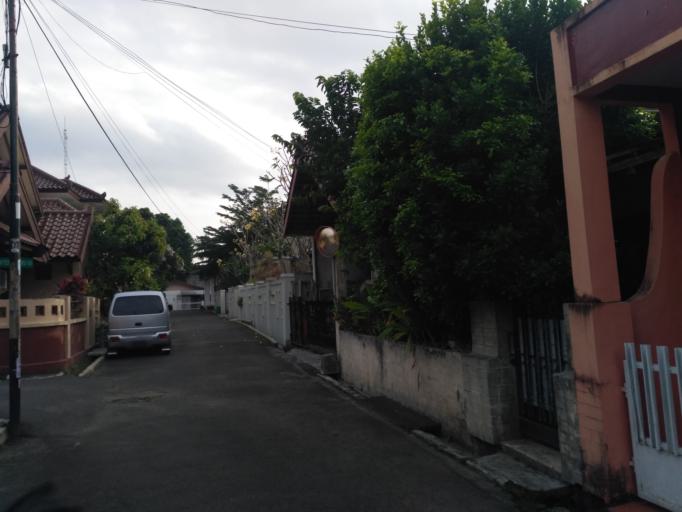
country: ID
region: Daerah Istimewa Yogyakarta
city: Melati
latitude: -7.7375
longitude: 110.3863
